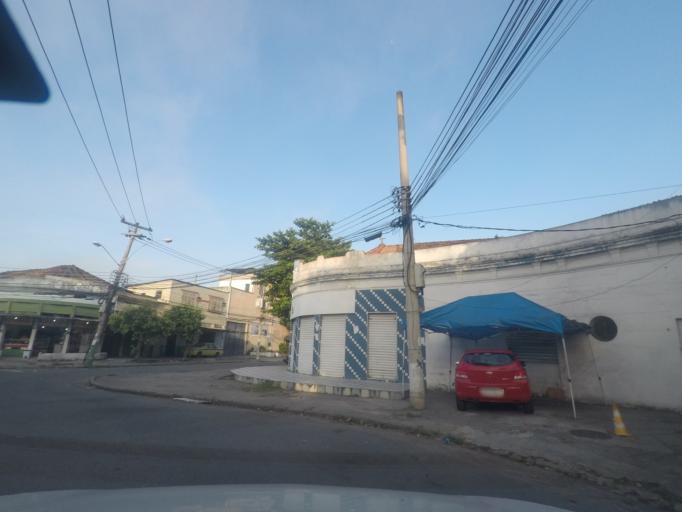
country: BR
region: Rio de Janeiro
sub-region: Duque De Caxias
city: Duque de Caxias
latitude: -22.8338
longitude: -43.2712
